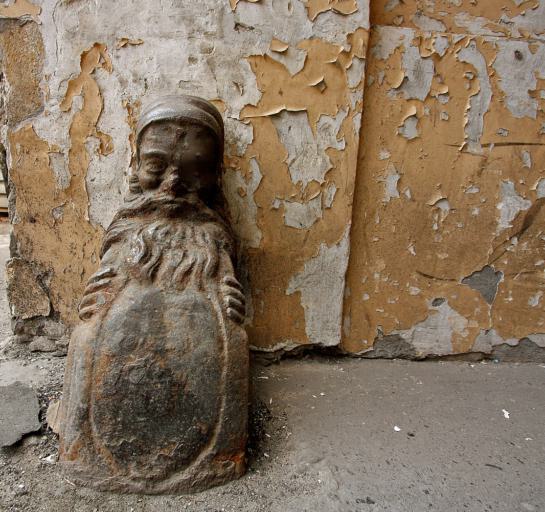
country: PL
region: Masovian Voivodeship
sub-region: Warszawa
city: Praga Polnoc
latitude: 52.2538
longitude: 21.0430
